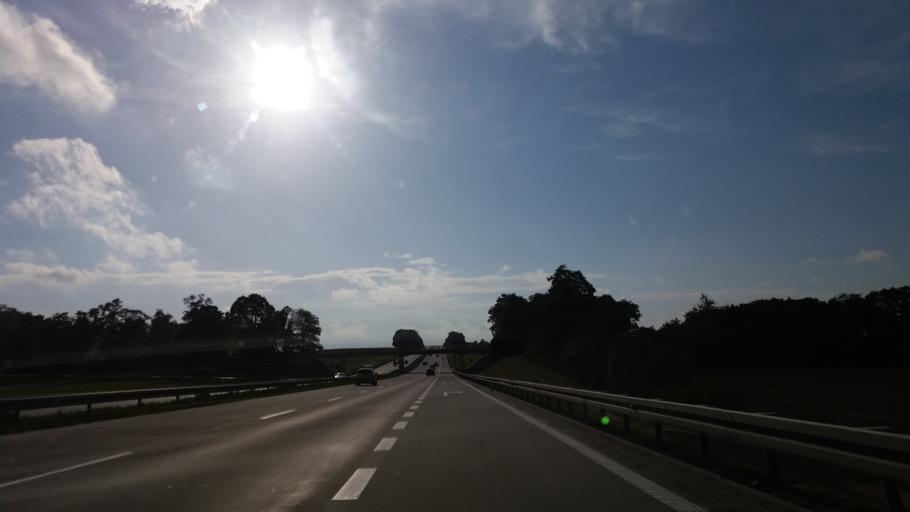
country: PL
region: Lower Silesian Voivodeship
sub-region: Powiat legnicki
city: Legnickie Pole
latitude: 51.1281
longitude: 16.3443
